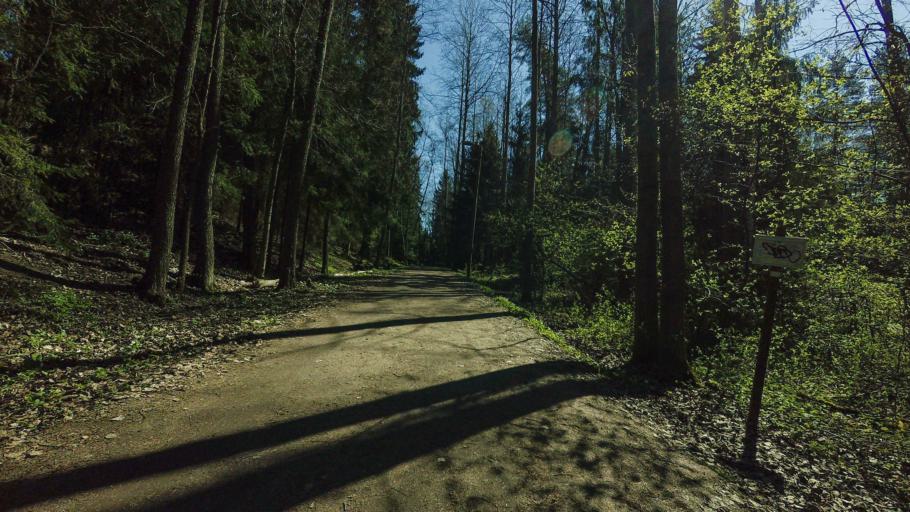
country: FI
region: Uusimaa
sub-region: Helsinki
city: Vantaa
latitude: 60.2357
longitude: 25.1393
